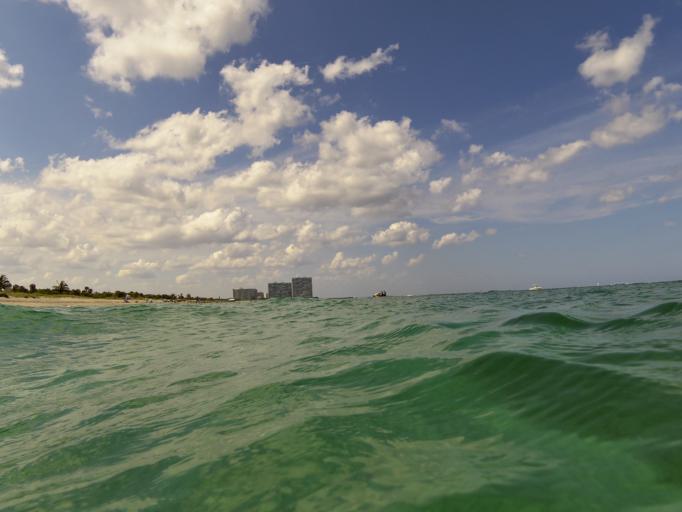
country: US
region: Florida
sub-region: Broward County
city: Dania Beach
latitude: 26.0785
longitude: -80.1092
